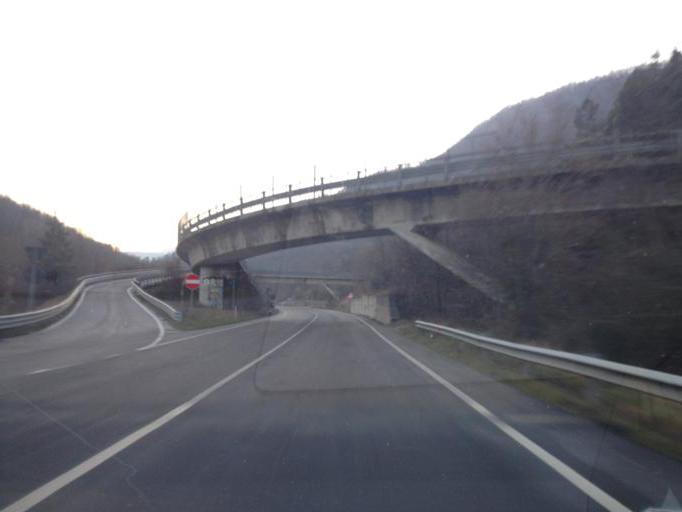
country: IT
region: The Marches
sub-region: Provincia di Ascoli Piceno
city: Arquata del Tronto
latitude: 42.7672
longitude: 13.2903
